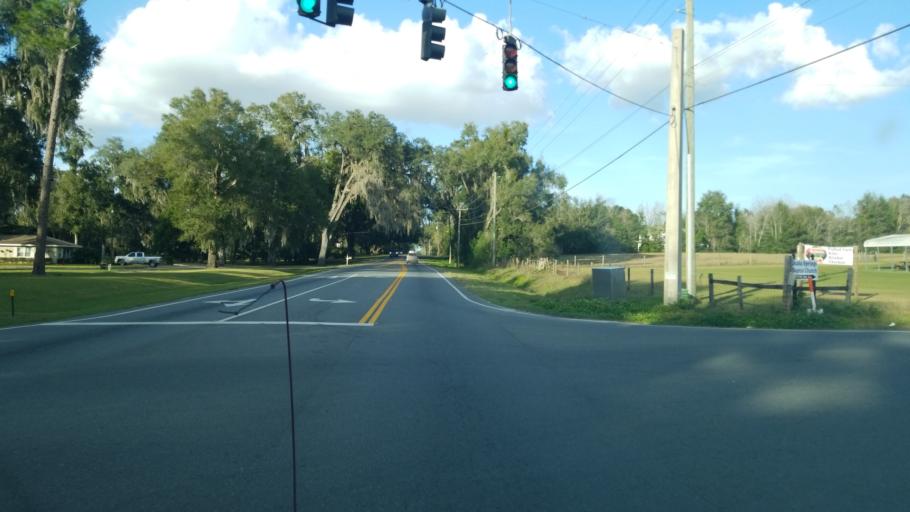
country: US
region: Florida
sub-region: Marion County
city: Ocala
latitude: 29.2375
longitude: -82.1199
